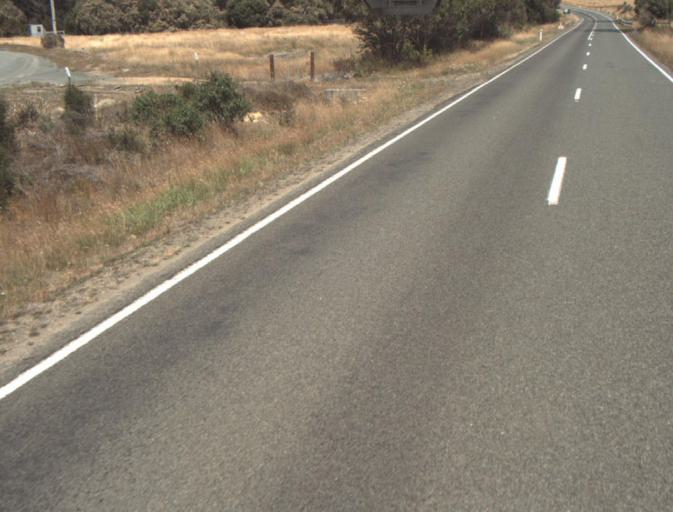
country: AU
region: Tasmania
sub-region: Launceston
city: Newstead
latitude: -41.3306
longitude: 147.3524
